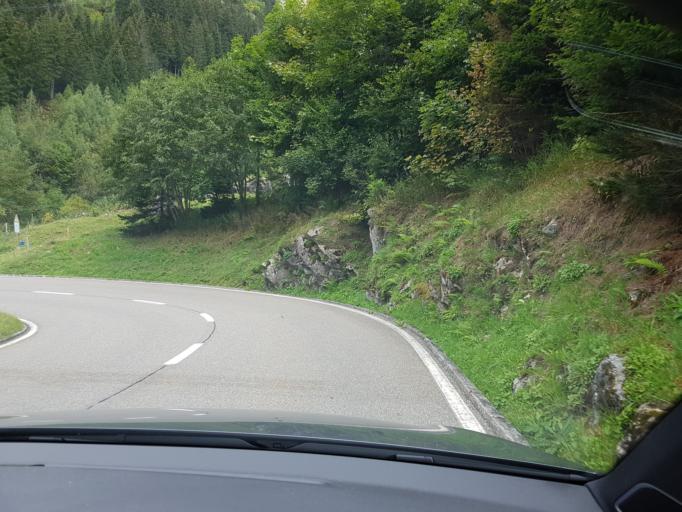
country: CH
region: Obwalden
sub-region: Obwalden
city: Engelberg
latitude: 46.7398
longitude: 8.3785
